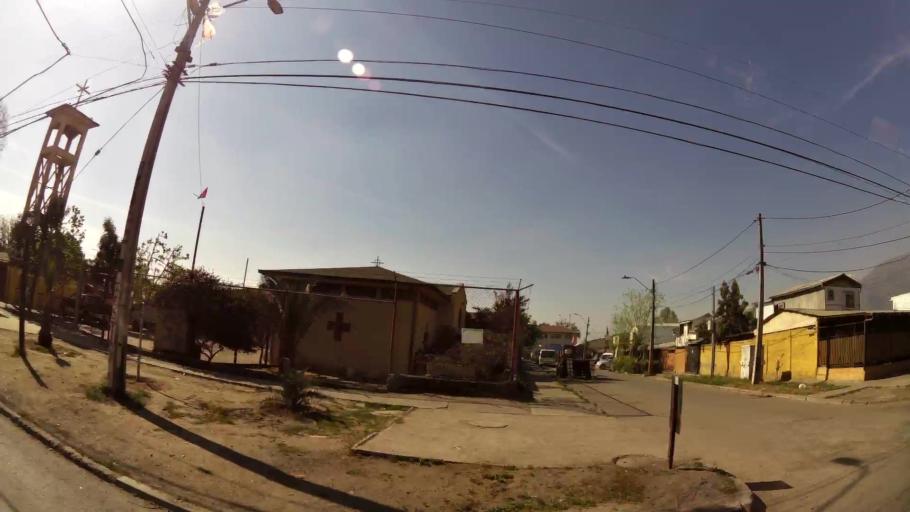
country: CL
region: Santiago Metropolitan
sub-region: Provincia de Santiago
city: Villa Presidente Frei, Nunoa, Santiago, Chile
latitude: -33.4781
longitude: -70.5653
